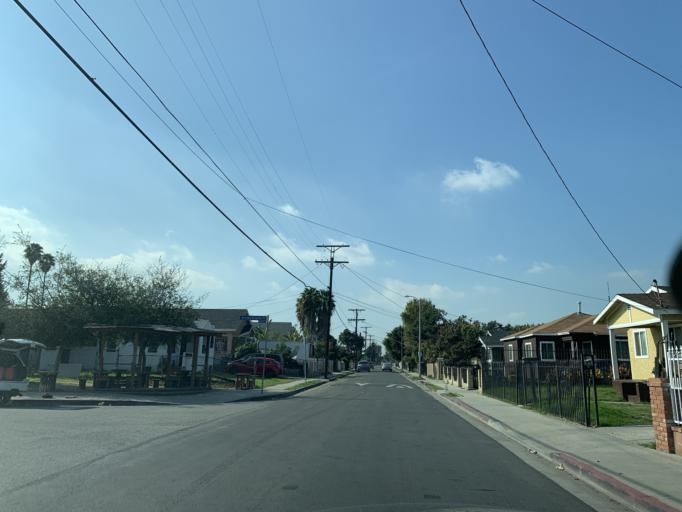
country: US
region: California
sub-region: Los Angeles County
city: Willowbrook
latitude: 33.9304
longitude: -118.2400
